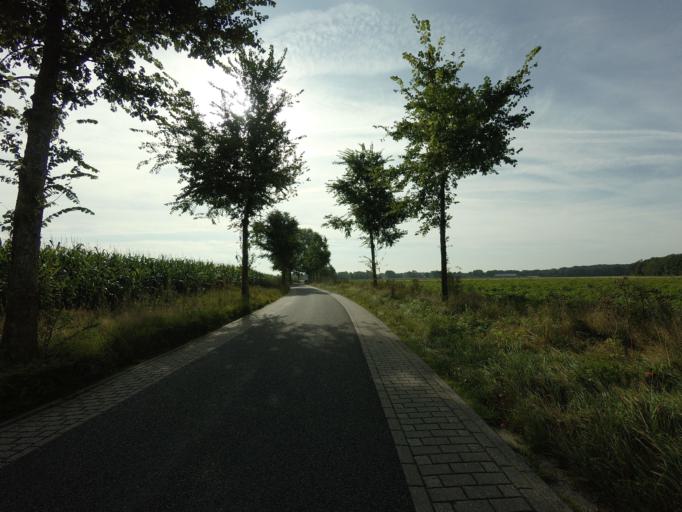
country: NL
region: Drenthe
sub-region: Gemeente Assen
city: Assen
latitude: 53.0011
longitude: 6.6251
